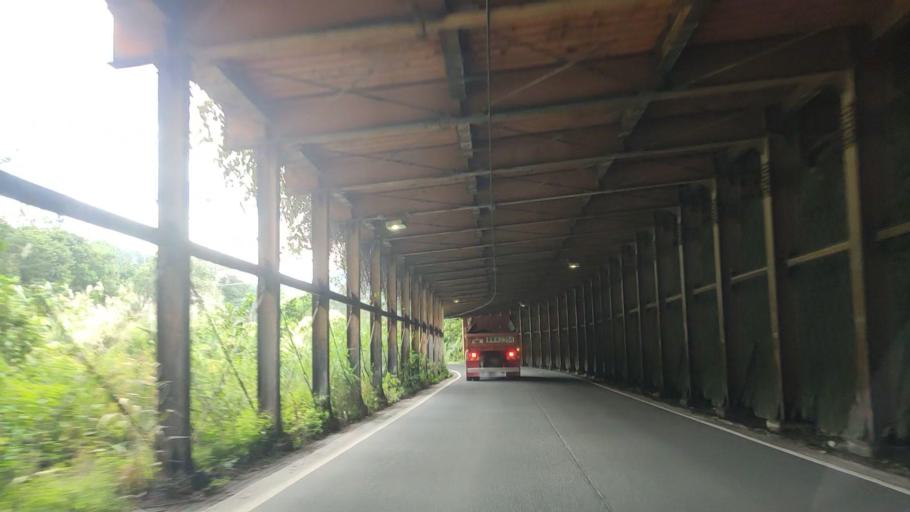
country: JP
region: Nagano
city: Iiyama
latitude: 36.8756
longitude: 138.3198
